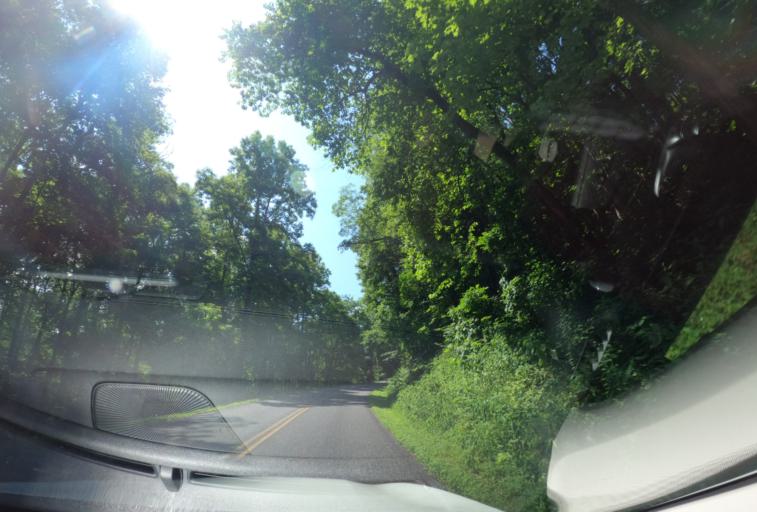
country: US
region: North Carolina
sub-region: Haywood County
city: Maggie Valley
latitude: 35.4415
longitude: -83.0849
